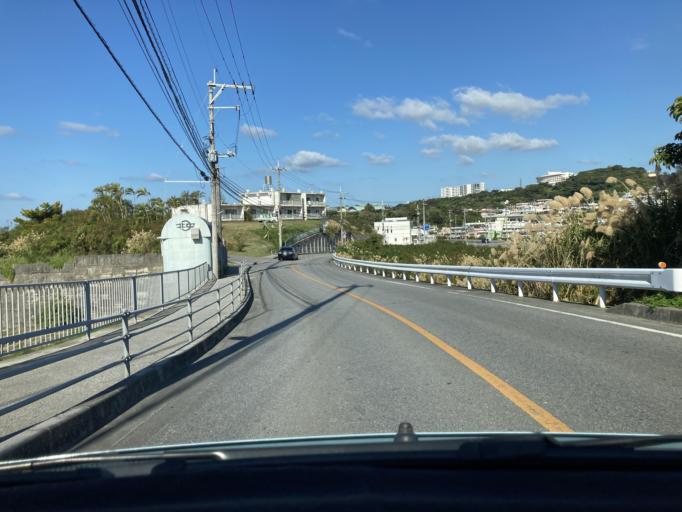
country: JP
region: Okinawa
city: Chatan
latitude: 26.2975
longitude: 127.7987
